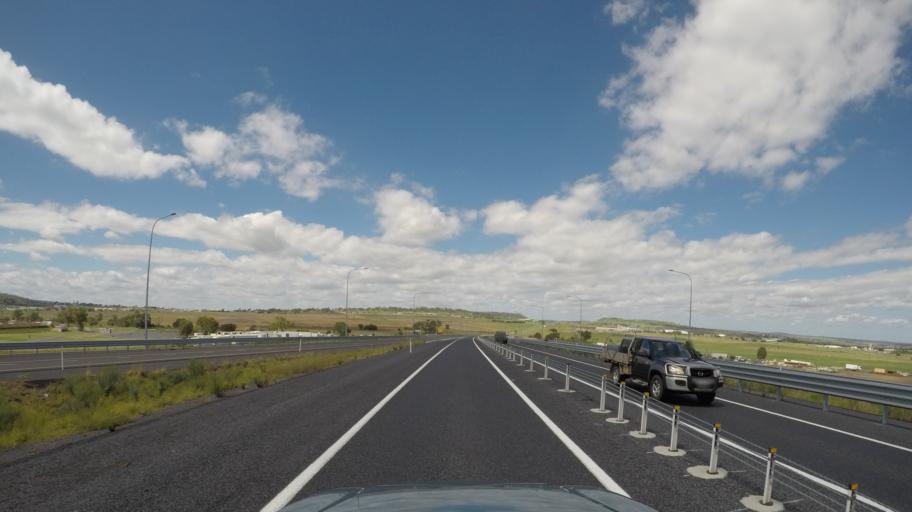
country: AU
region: Queensland
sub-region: Toowoomba
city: Wilsonton Heights
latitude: -27.5281
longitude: 151.8587
